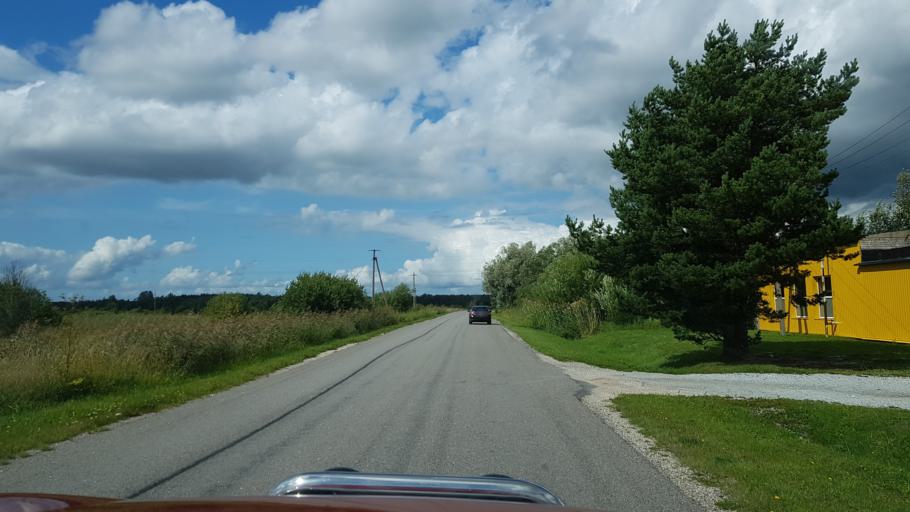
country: EE
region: Laeaene
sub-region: Lihula vald
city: Lihula
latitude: 58.6935
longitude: 23.8341
